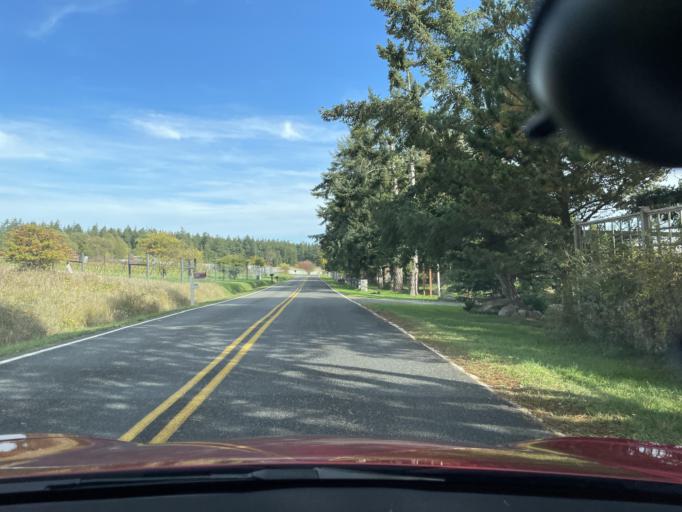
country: US
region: Washington
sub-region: San Juan County
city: Friday Harbor
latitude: 48.5187
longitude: -122.9811
